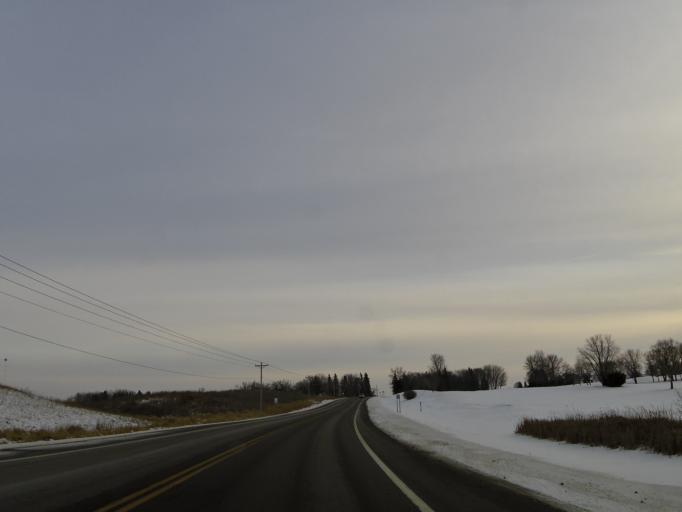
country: US
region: Minnesota
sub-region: Carver County
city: Victoria
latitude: 44.8477
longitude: -93.6555
